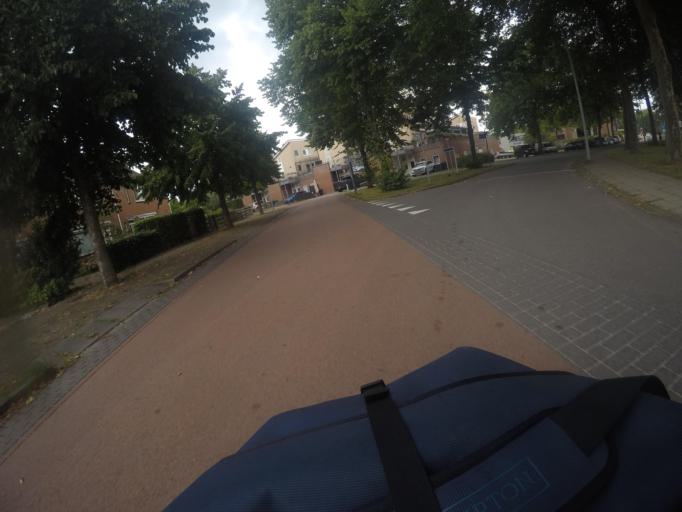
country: NL
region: Flevoland
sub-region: Gemeente Almere
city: Almere Stad
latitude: 52.3459
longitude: 5.2184
